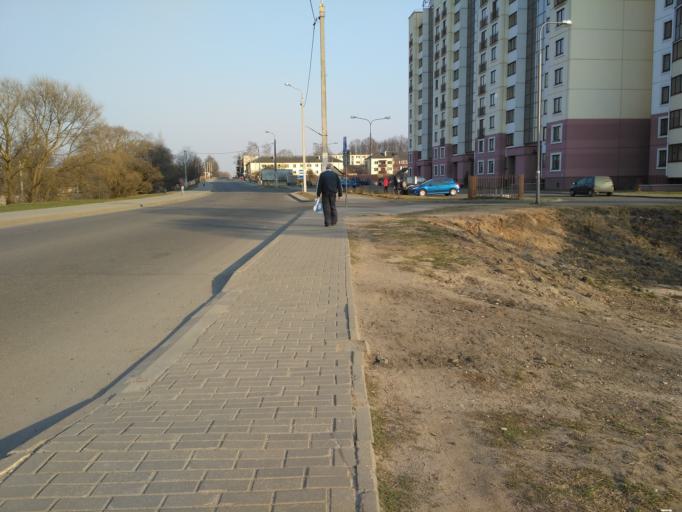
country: BY
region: Minsk
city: Zaslawye
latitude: 54.0089
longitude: 27.2756
